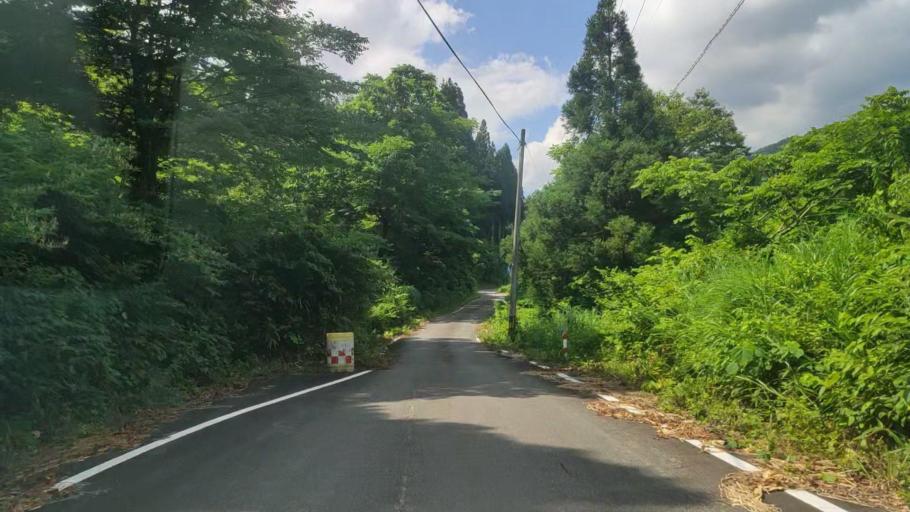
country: JP
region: Fukui
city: Katsuyama
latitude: 36.2128
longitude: 136.5285
